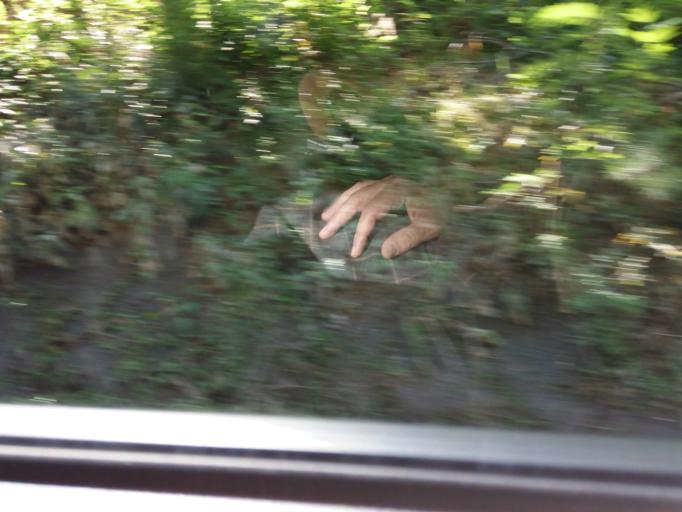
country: US
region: Tennessee
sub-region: Sevier County
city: Gatlinburg
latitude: 35.7118
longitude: -83.5386
